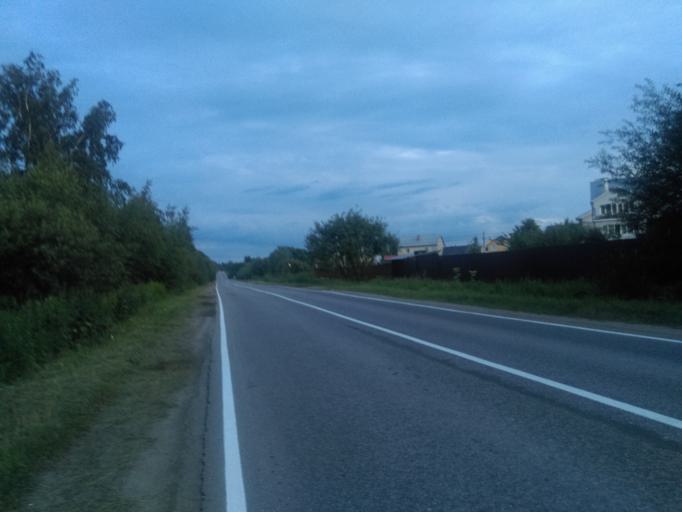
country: RU
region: Moskovskaya
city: Vostryakovo
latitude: 55.3910
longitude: 37.8071
